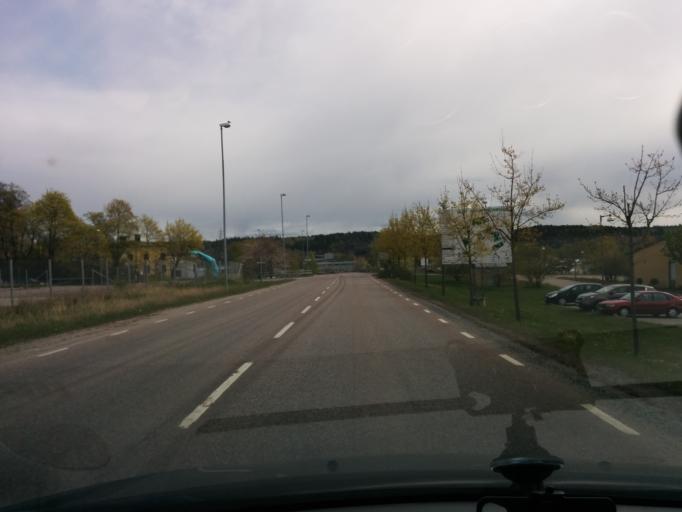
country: SE
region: Stockholm
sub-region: Botkyrka Kommun
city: Alby
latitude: 59.2387
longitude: 17.8554
